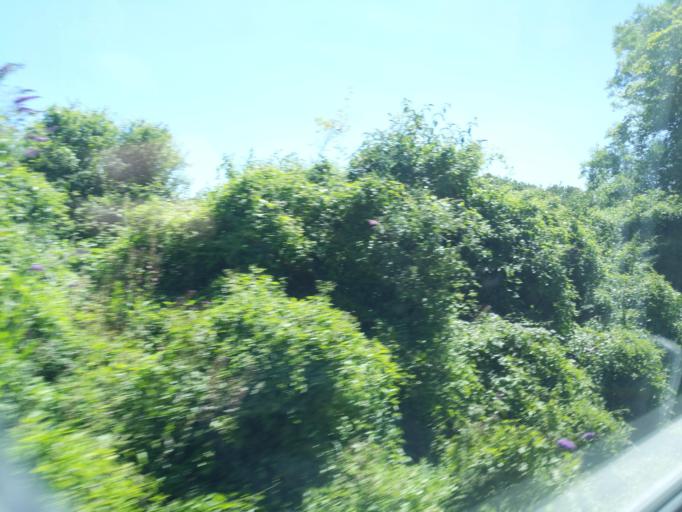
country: GB
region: England
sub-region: Cornwall
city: Hayle
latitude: 50.1726
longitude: -5.4372
